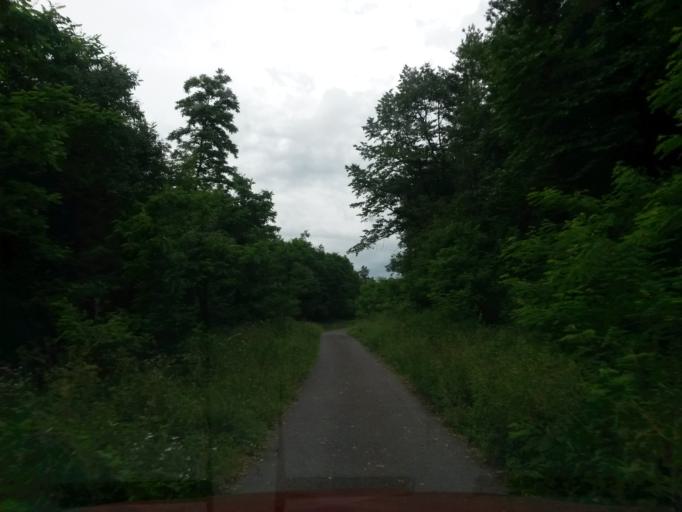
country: SK
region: Banskobystricky
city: Velky Krtis
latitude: 48.3047
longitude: 19.4087
